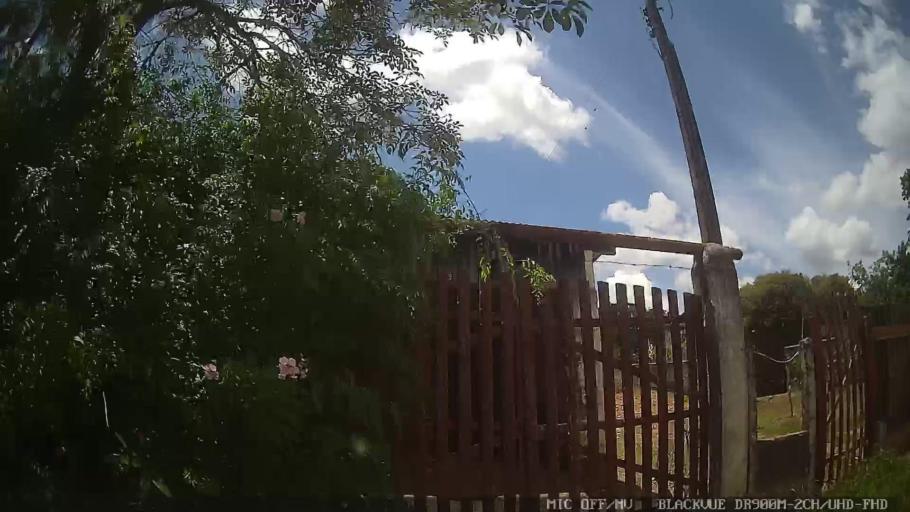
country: BR
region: Sao Paulo
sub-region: Atibaia
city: Atibaia
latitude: -23.0389
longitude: -46.5374
